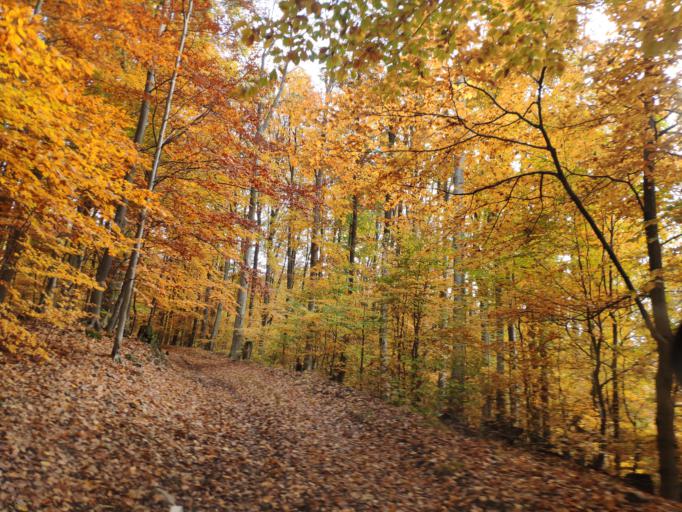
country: SK
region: Kosicky
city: Medzev
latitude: 48.7345
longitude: 20.9888
